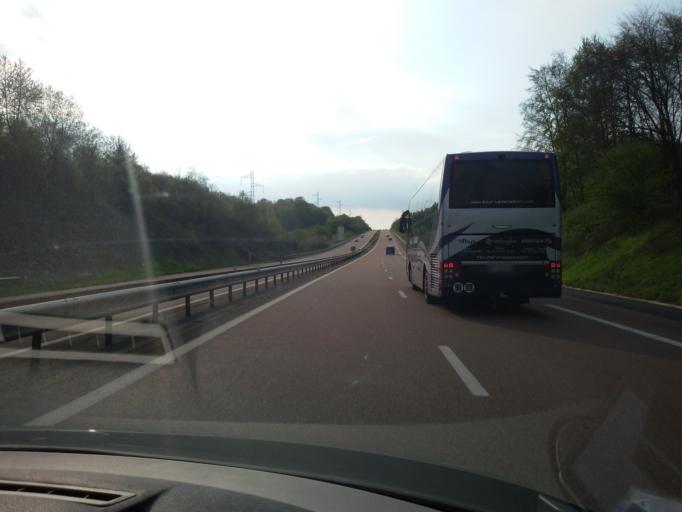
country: FR
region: Champagne-Ardenne
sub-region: Departement de l'Aube
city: Ville-sous-la-Ferte
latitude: 48.1184
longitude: 4.7290
